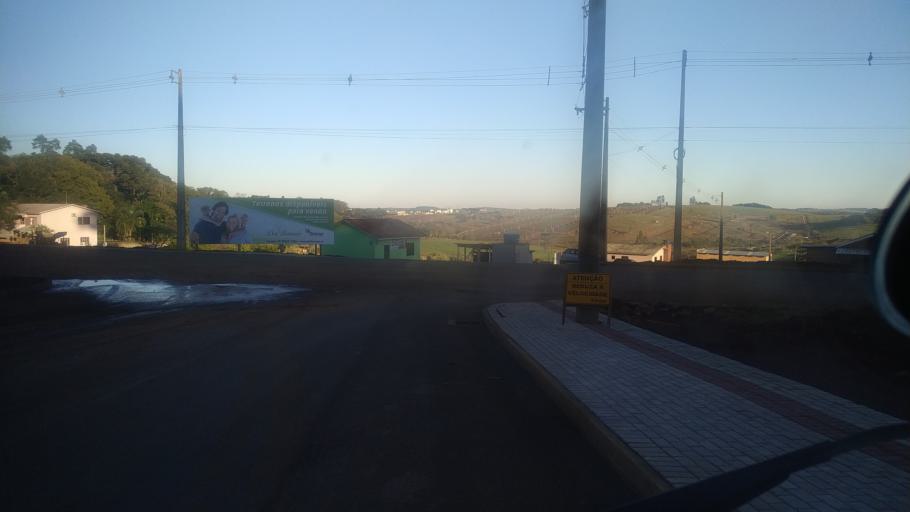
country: BR
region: Santa Catarina
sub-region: Chapeco
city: Chapeco
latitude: -27.0901
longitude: -52.6929
